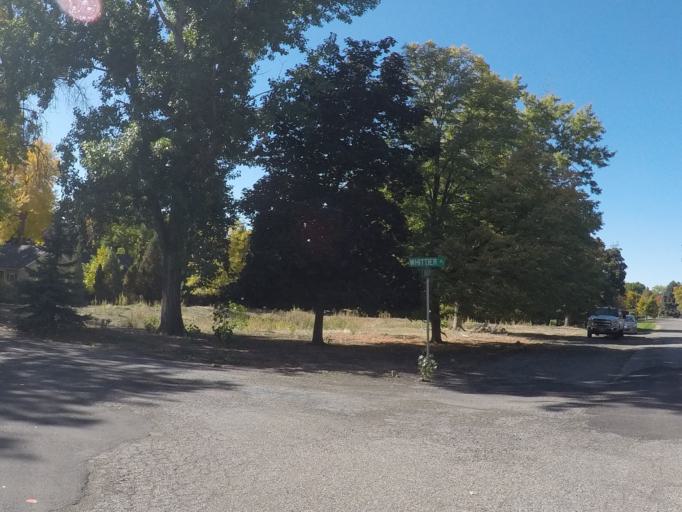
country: US
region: Montana
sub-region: Yellowstone County
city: Billings
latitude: 45.7968
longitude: -108.5322
